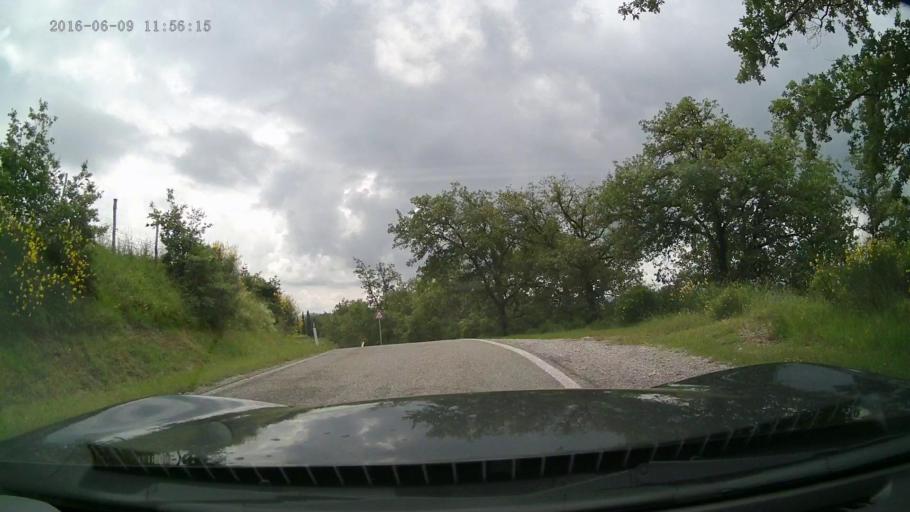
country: IT
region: Tuscany
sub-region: Province of Florence
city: Panzano in Chianti
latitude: 43.5618
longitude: 11.2956
